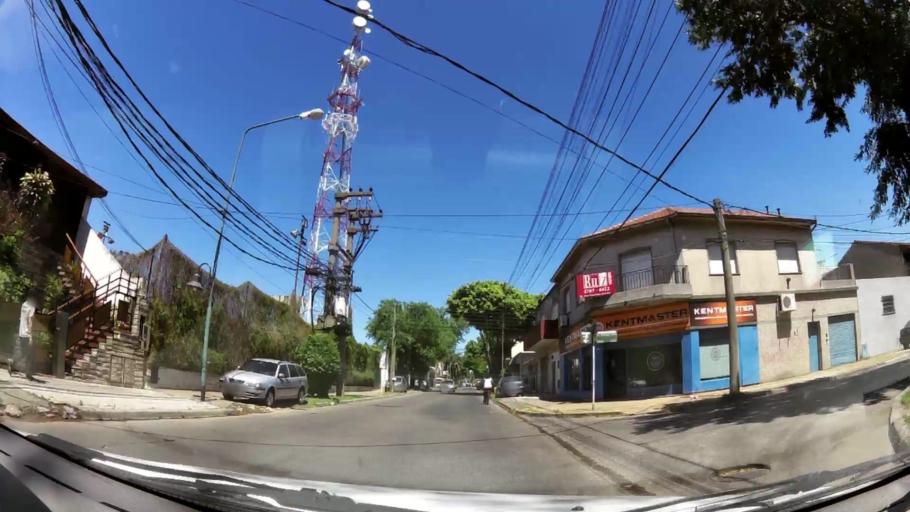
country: AR
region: Buenos Aires
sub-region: Partido de Vicente Lopez
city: Olivos
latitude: -34.5133
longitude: -58.5137
